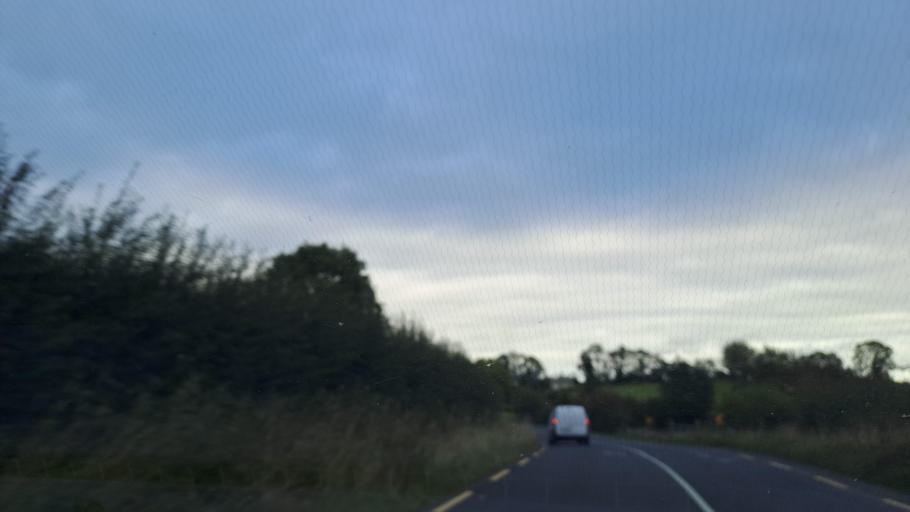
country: IE
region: Ulster
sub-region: County Monaghan
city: Monaghan
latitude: 54.1163
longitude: -6.9109
